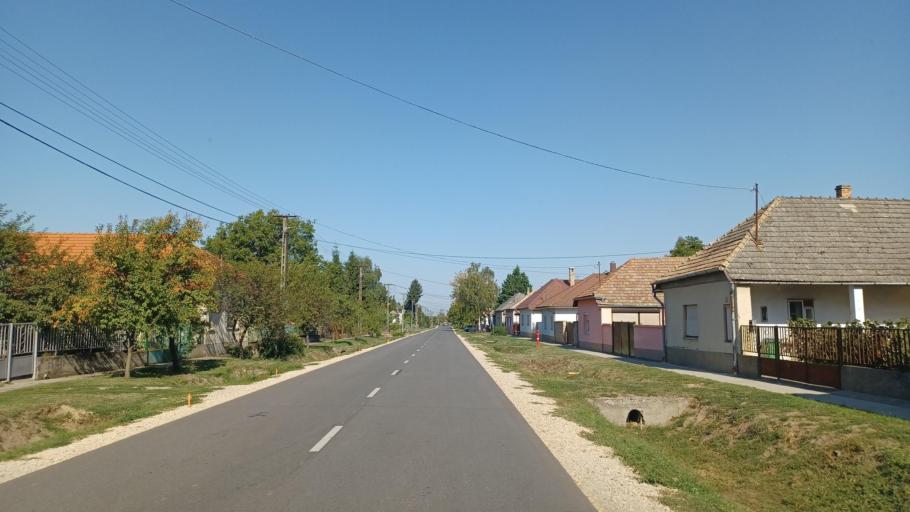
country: HU
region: Tolna
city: Nemetker
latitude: 46.7239
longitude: 18.7560
